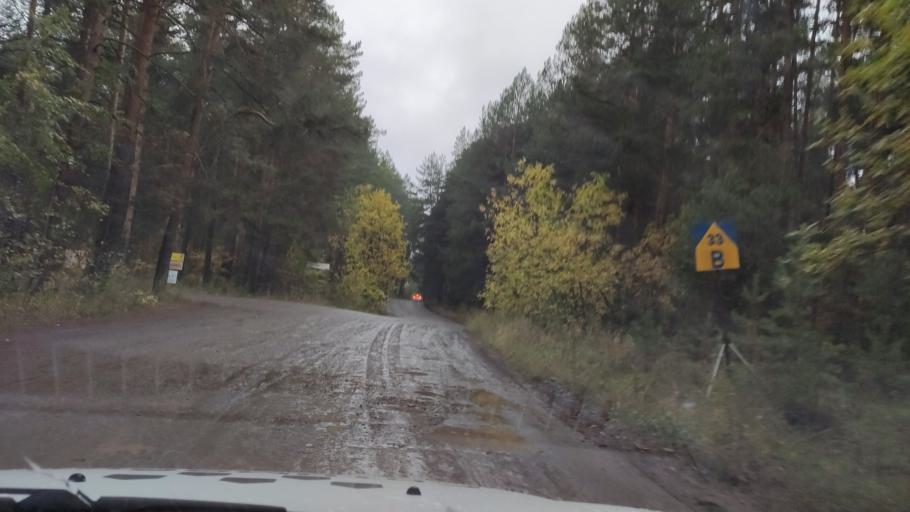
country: RU
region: Perm
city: Kondratovo
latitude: 58.0437
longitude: 56.1664
